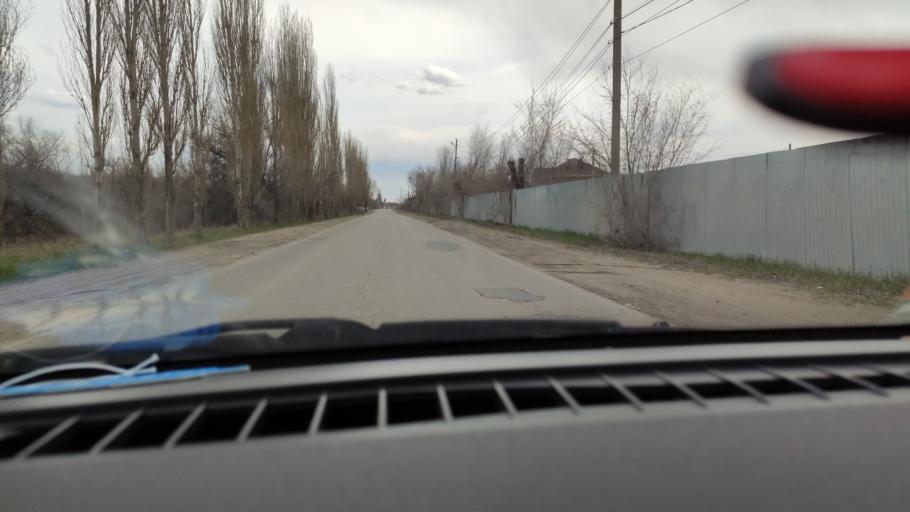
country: RU
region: Saratov
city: Engel's
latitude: 51.4810
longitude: 46.0566
